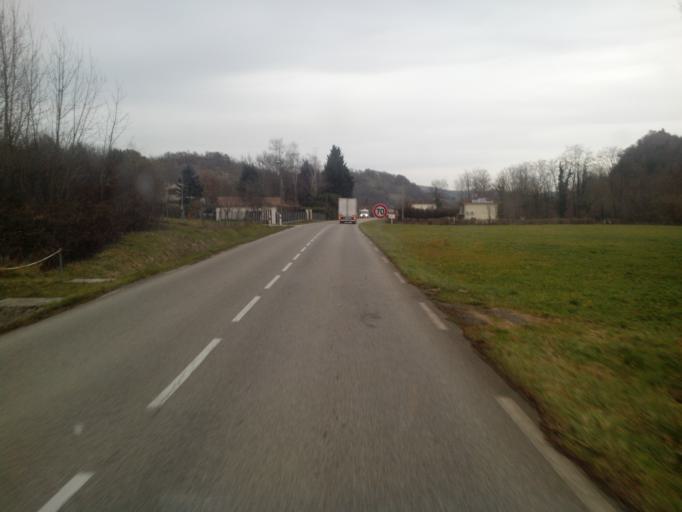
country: FR
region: Midi-Pyrenees
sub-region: Departement de l'Ariege
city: Montjoie-en-Couserans
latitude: 42.9974
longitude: 1.3294
